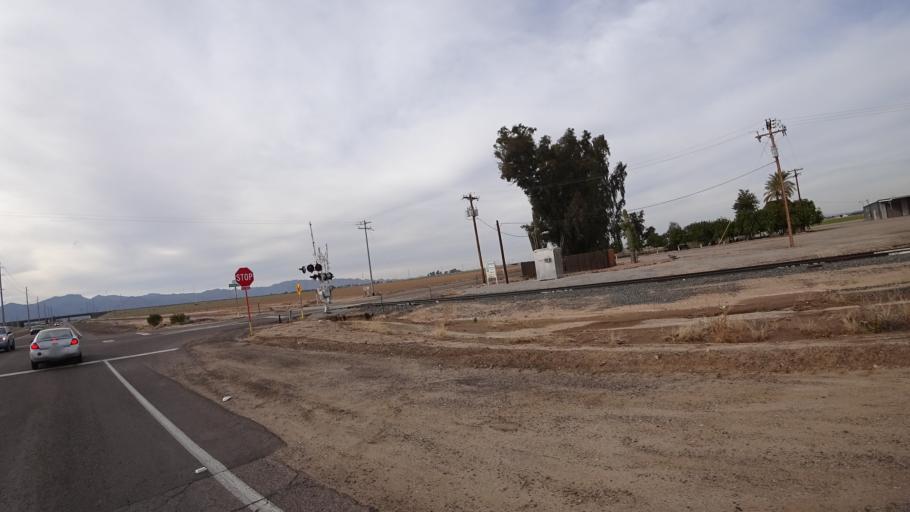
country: US
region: Arizona
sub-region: Maricopa County
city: Citrus Park
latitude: 33.5663
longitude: -112.4092
